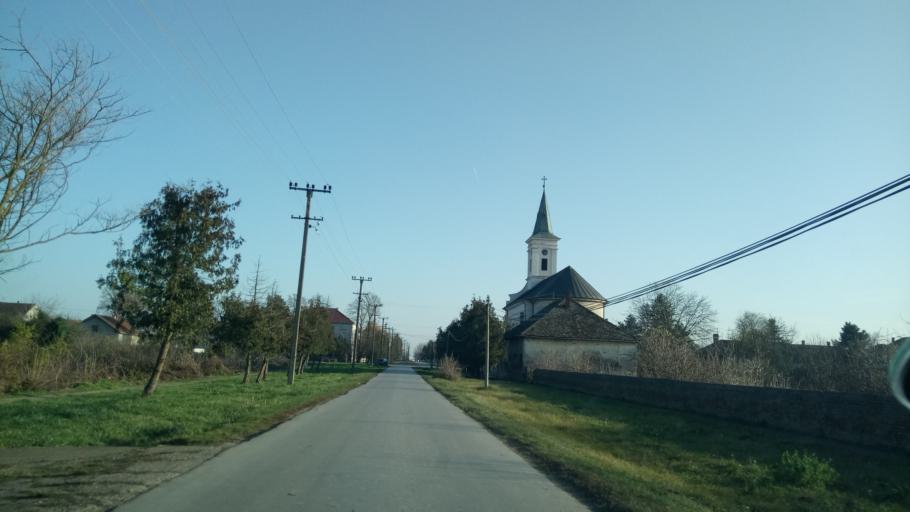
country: RS
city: Novi Slankamen
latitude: 45.1254
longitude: 20.2355
